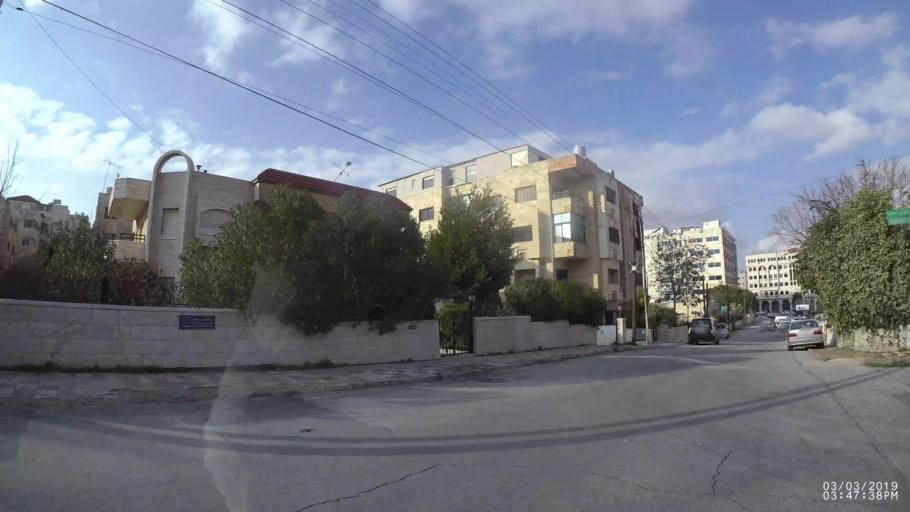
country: JO
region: Amman
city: Al Jubayhah
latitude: 31.9861
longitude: 35.8756
